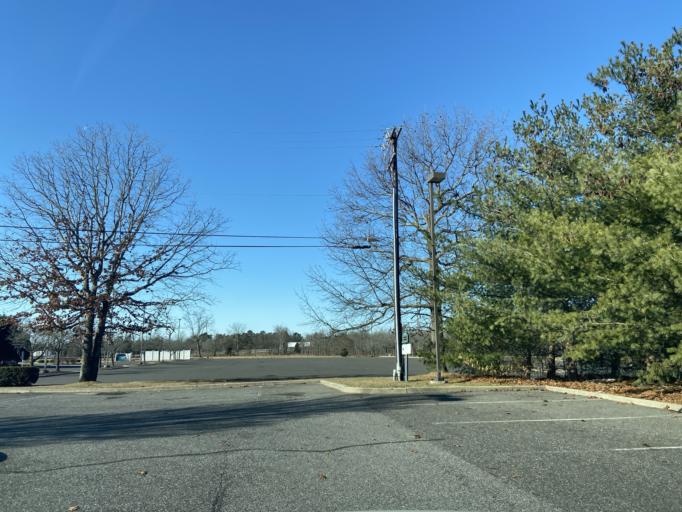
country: US
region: New Jersey
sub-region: Cumberland County
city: Vineland
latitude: 39.4898
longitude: -75.0669
